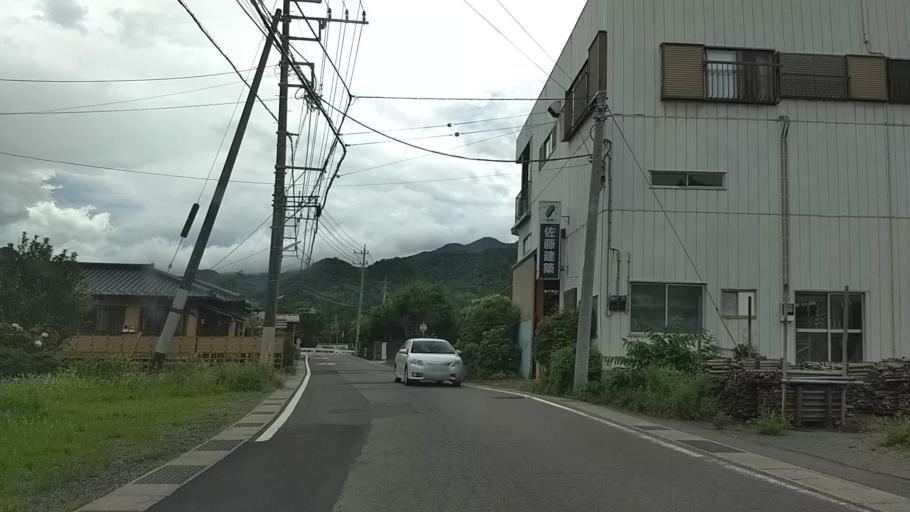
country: JP
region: Yamanashi
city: Otsuki
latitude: 35.5659
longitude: 138.9338
